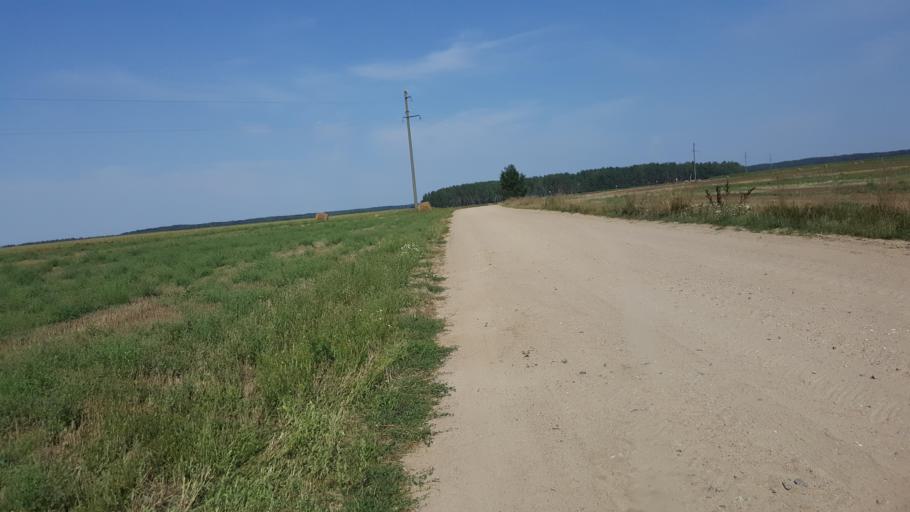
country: BY
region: Brest
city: Kamyanyuki
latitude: 52.4974
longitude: 23.6045
